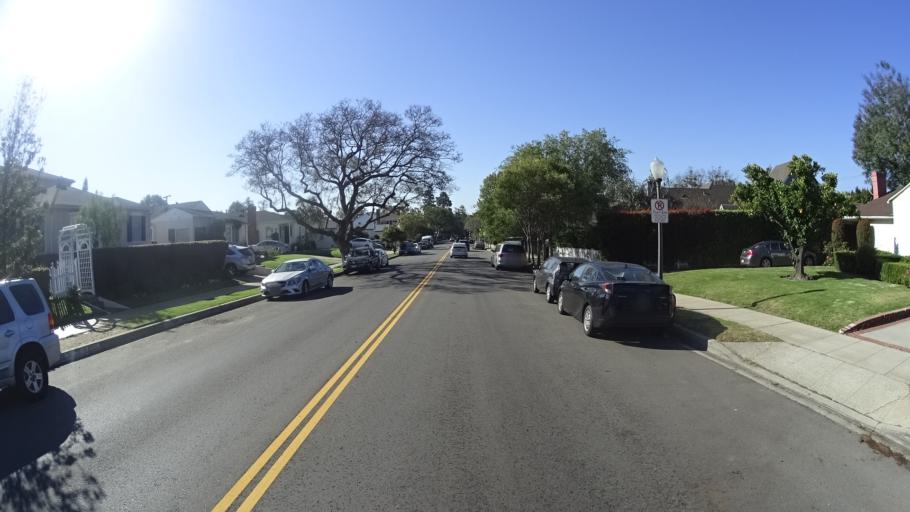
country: US
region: California
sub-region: Los Angeles County
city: Santa Monica
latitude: 34.0577
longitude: -118.4777
